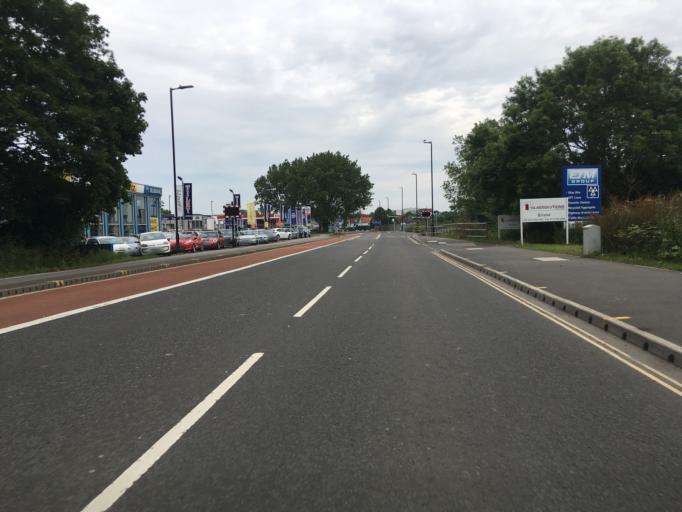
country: GB
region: England
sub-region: Bristol
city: Bristol
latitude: 51.4266
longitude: -2.6043
